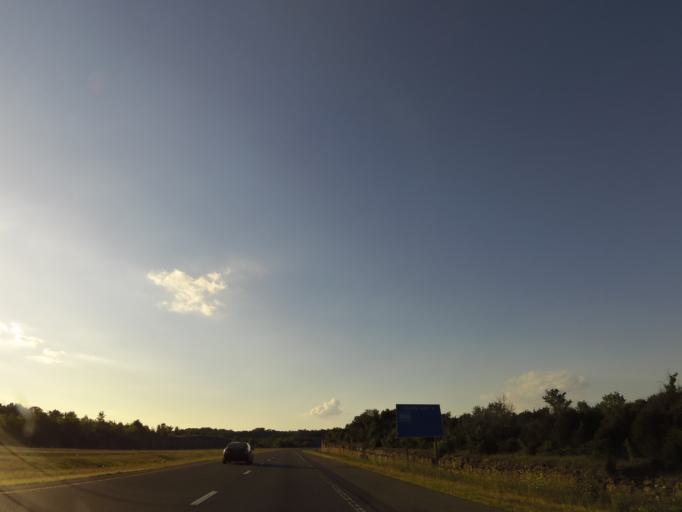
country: US
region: Tennessee
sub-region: Rutherford County
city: Smyrna
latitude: 35.9626
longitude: -86.4471
